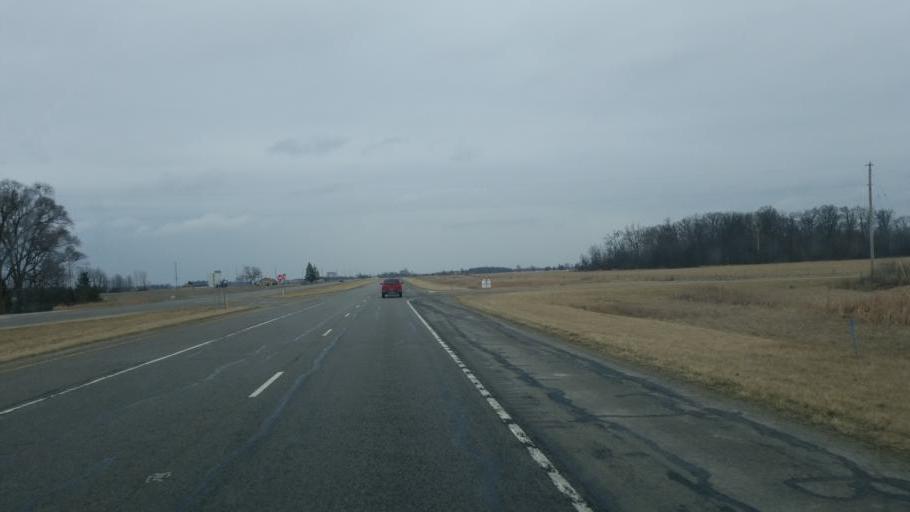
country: US
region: Indiana
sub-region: Adams County
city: Decatur
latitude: 40.7748
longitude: -84.9376
